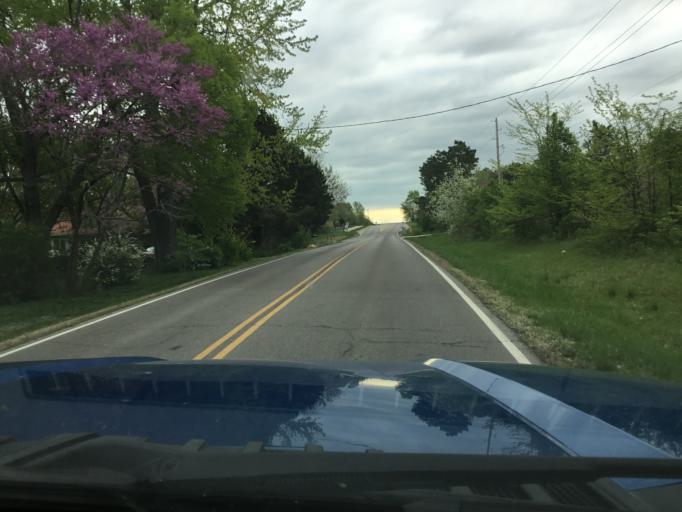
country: US
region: Kansas
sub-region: Douglas County
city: Lawrence
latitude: 38.9861
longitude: -95.2931
